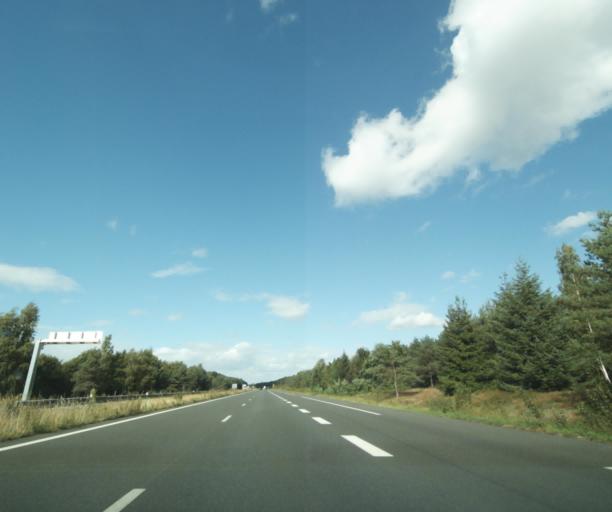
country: FR
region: Centre
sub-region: Departement du Loiret
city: Saint-Hilaire-Saint-Mesmin
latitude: 47.8117
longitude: 1.8550
